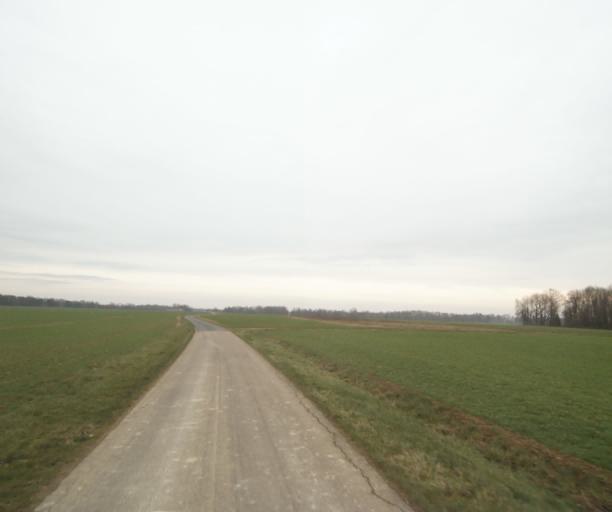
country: FR
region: Champagne-Ardenne
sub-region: Departement de la Haute-Marne
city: Villiers-en-Lieu
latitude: 48.6375
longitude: 4.7977
